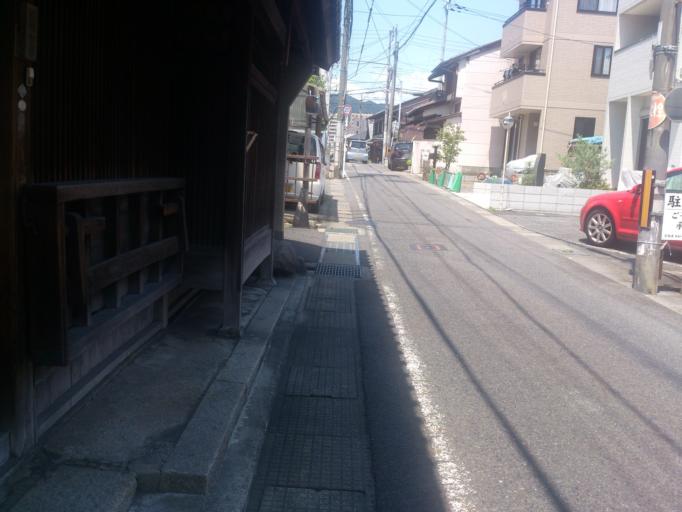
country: JP
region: Shiga Prefecture
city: Otsu-shi
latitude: 35.0046
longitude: 135.8724
